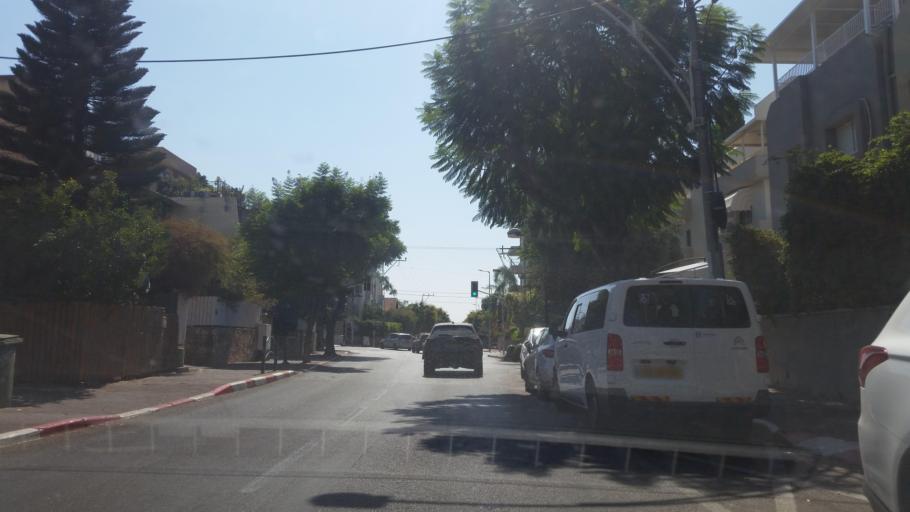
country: IL
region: Central District
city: Ra'anana
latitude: 32.1789
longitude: 34.8846
